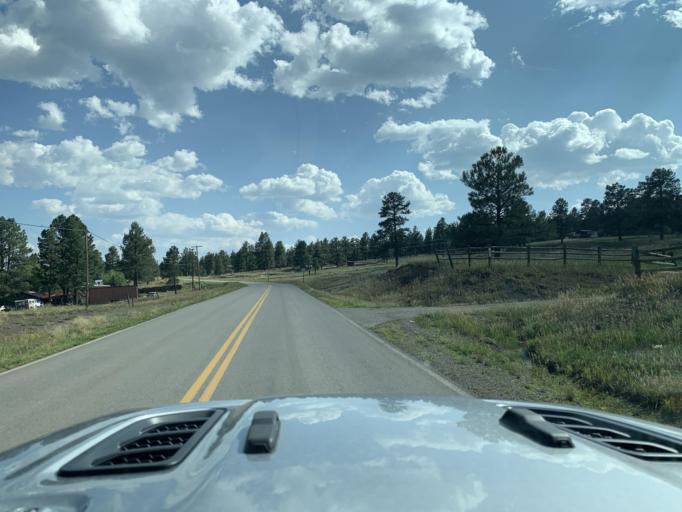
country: US
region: Colorado
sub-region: Archuleta County
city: Pagosa Springs
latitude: 37.2534
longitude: -107.0246
